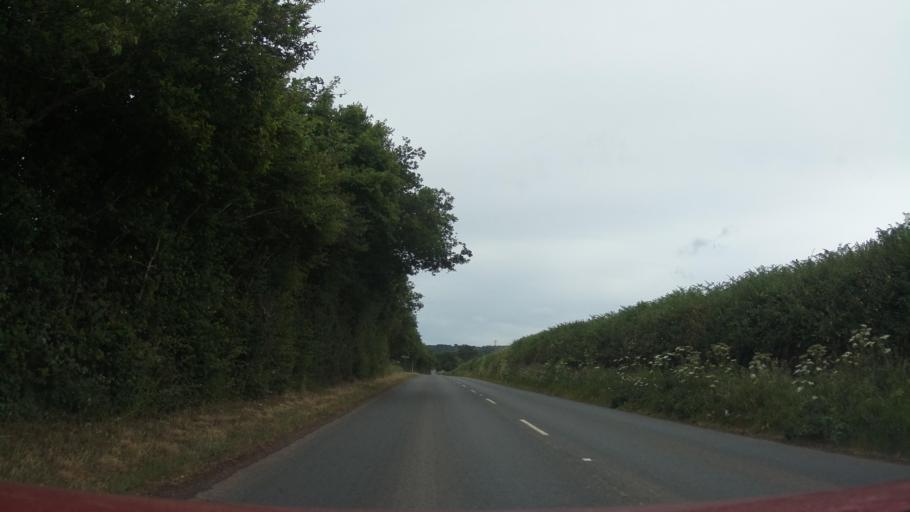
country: GB
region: England
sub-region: Devon
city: Bradninch
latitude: 50.7526
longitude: -3.3729
